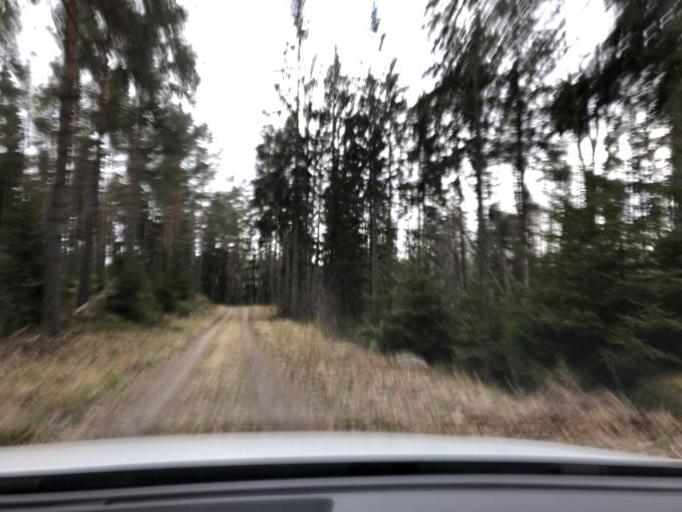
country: SE
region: Gaevleborg
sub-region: Gavle Kommun
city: Hedesunda
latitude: 60.3442
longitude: 17.0612
